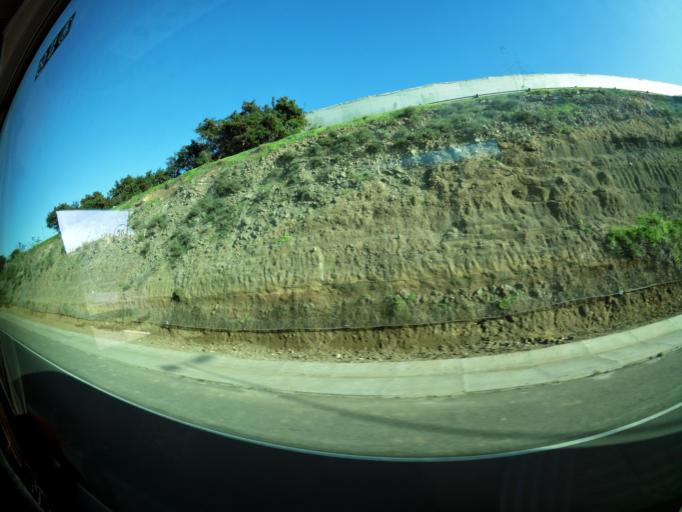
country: ES
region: Canary Islands
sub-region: Provincia de Las Palmas
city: Galdar
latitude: 28.1315
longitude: -15.6556
